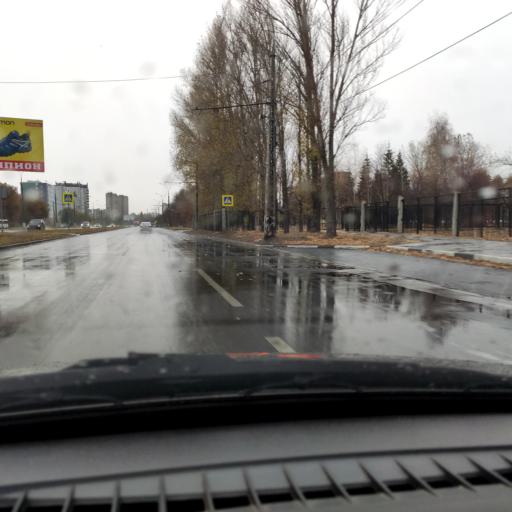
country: RU
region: Samara
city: Tol'yatti
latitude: 53.4991
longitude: 49.2985
